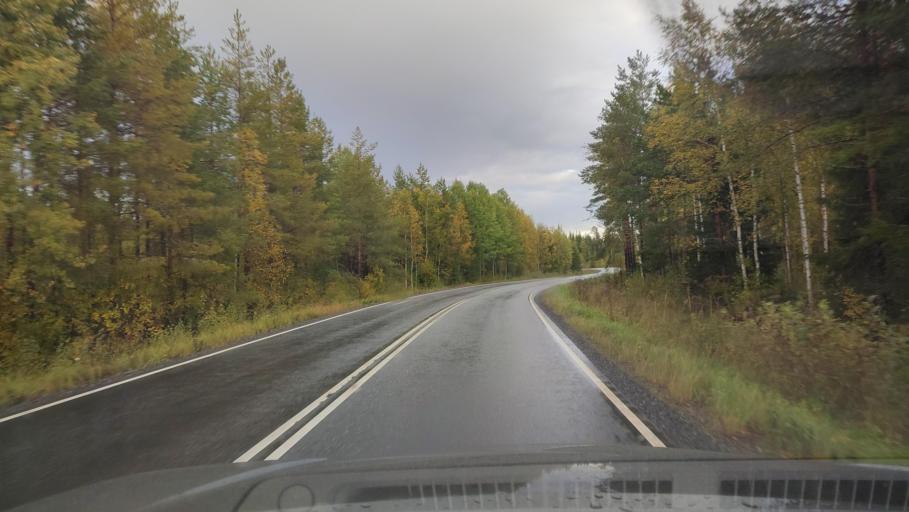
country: FI
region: Southern Ostrobothnia
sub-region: Suupohja
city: Karijoki
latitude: 62.2764
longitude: 21.5840
